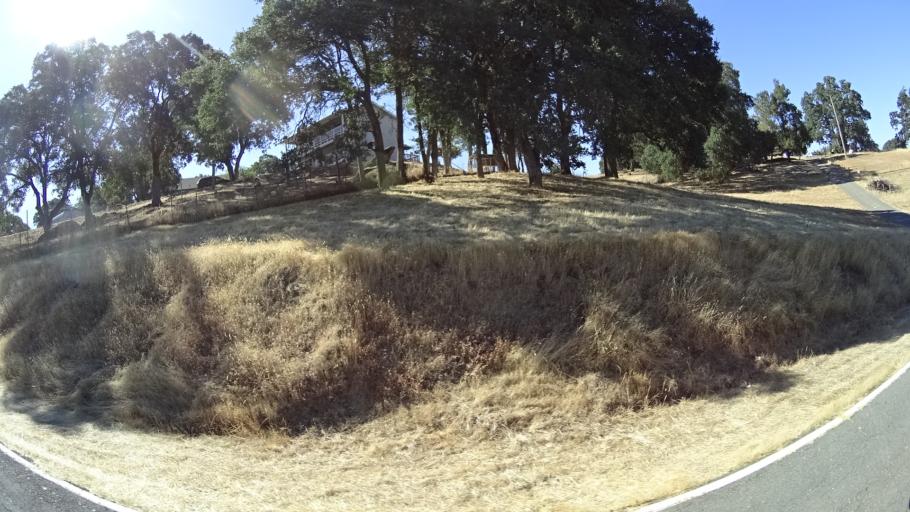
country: US
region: California
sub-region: Calaveras County
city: Rancho Calaveras
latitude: 38.0952
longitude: -120.8645
